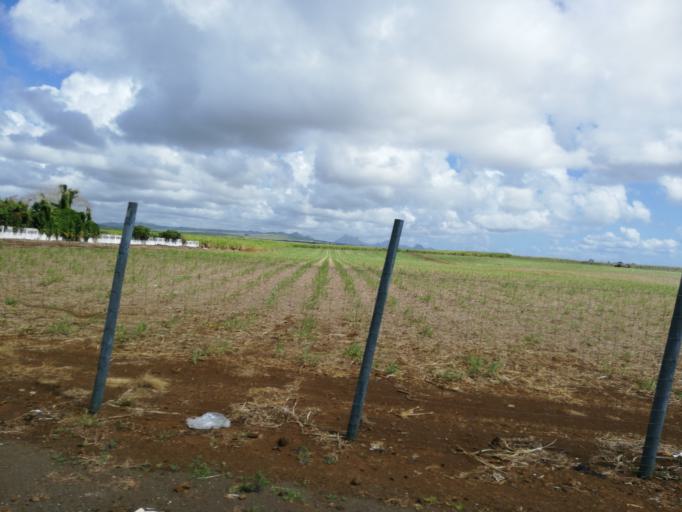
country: MU
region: Riviere du Rempart
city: Goodlands
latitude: -20.0501
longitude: 57.6657
